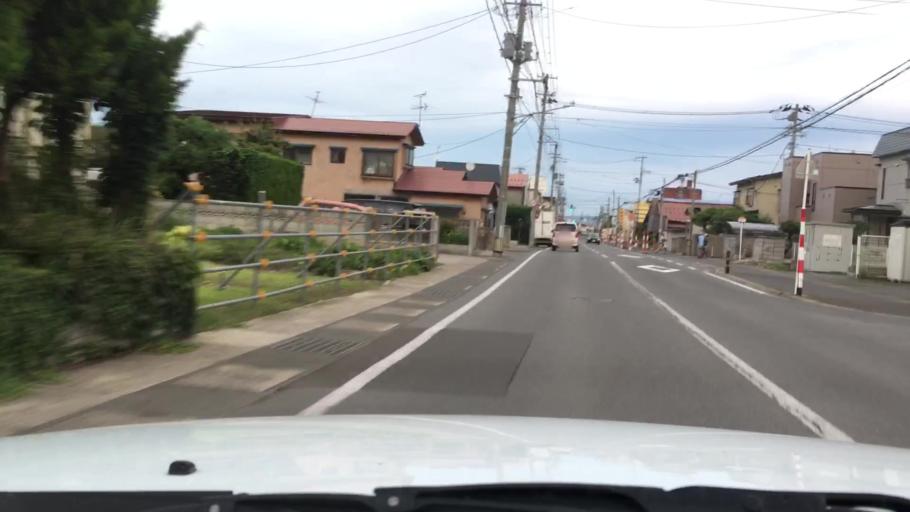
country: JP
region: Aomori
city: Hirosaki
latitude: 40.5881
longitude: 140.4800
